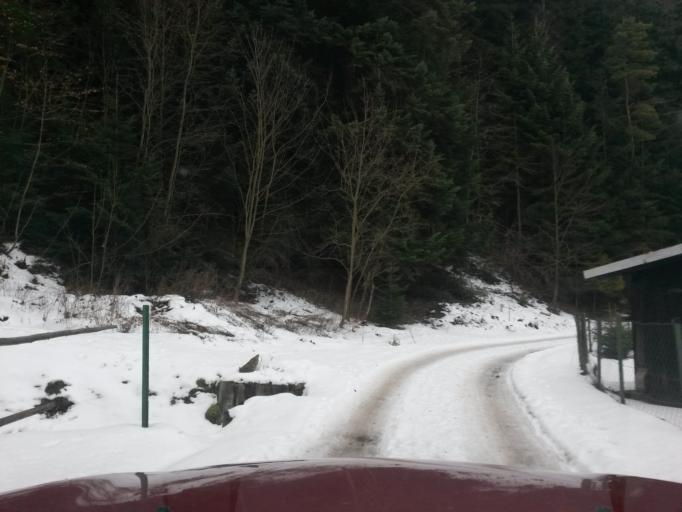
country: SK
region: Kosicky
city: Spisska Nova Ves
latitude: 48.8715
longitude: 20.5789
